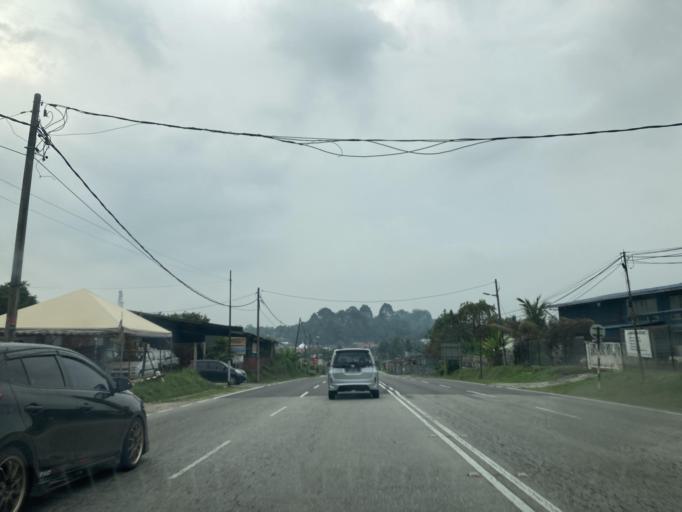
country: MY
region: Selangor
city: Kuang
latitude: 3.2090
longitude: 101.5377
